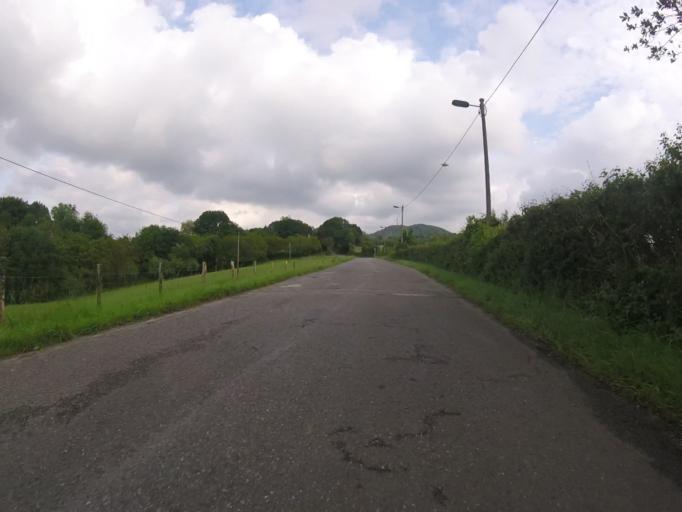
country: ES
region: Basque Country
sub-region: Provincia de Guipuzcoa
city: Pasaia
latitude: 43.3043
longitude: -1.9359
